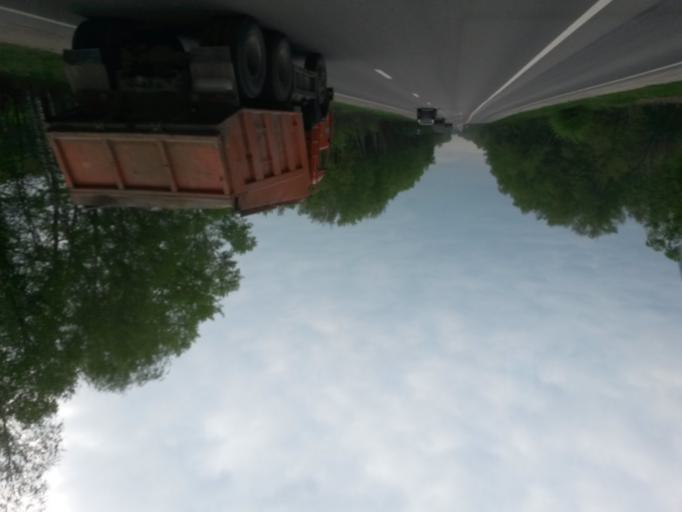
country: RU
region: Moskovskaya
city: Barybino
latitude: 55.2094
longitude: 37.8681
